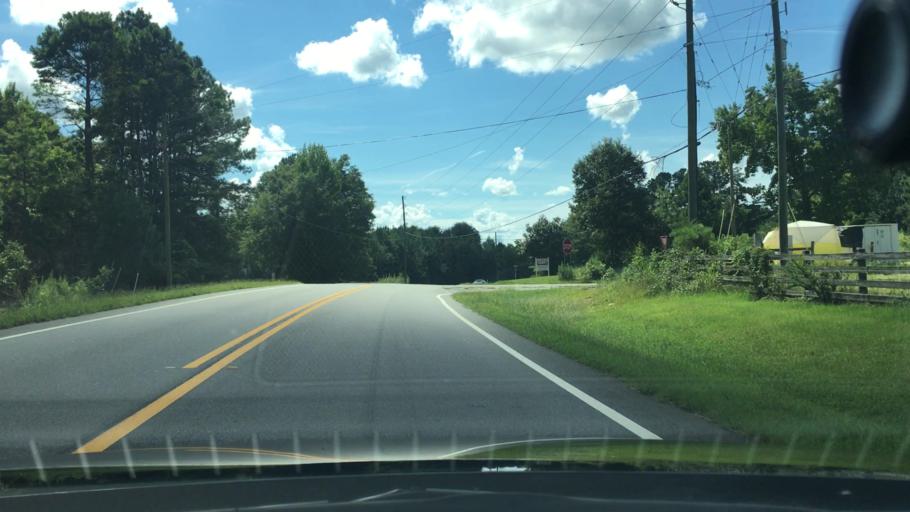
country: US
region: Georgia
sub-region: Butts County
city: Jackson
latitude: 33.2891
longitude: -83.9377
